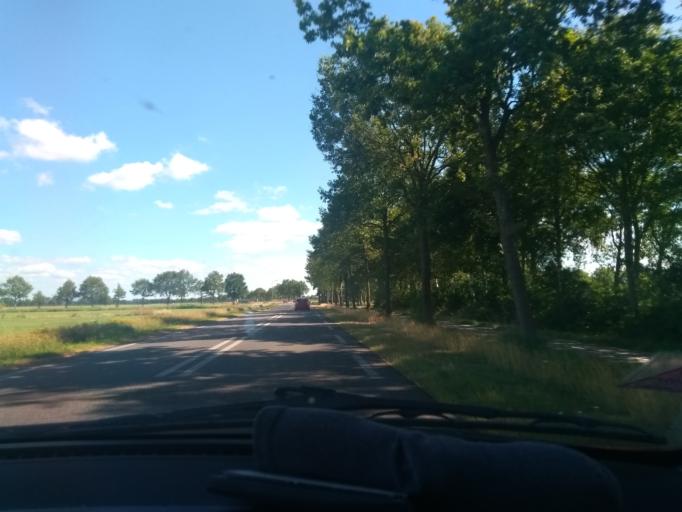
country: NL
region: Drenthe
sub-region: Gemeente Tynaarlo
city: Vries
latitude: 53.1283
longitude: 6.5010
